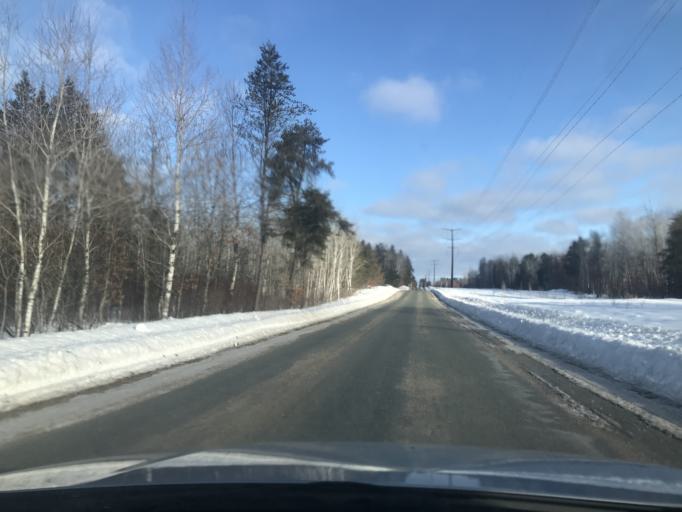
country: US
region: Wisconsin
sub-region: Marinette County
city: Niagara
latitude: 45.5932
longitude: -87.9769
